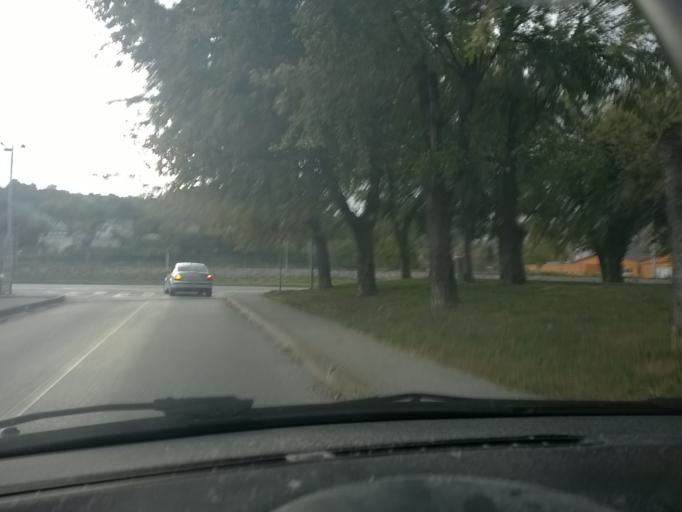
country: HR
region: Krapinsko-Zagorska
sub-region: Grad Krapina
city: Krapina
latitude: 46.1540
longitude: 15.8742
